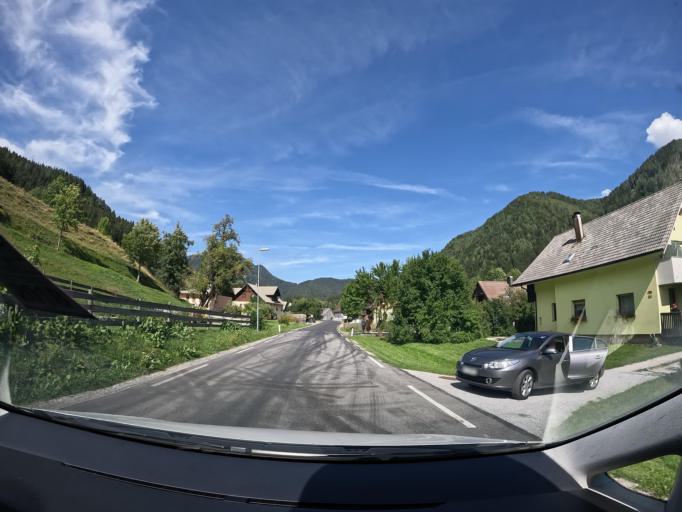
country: AT
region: Carinthia
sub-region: Politischer Bezirk Feldkirchen
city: Feldkirchen in Karnten
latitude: 46.6875
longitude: 14.1244
